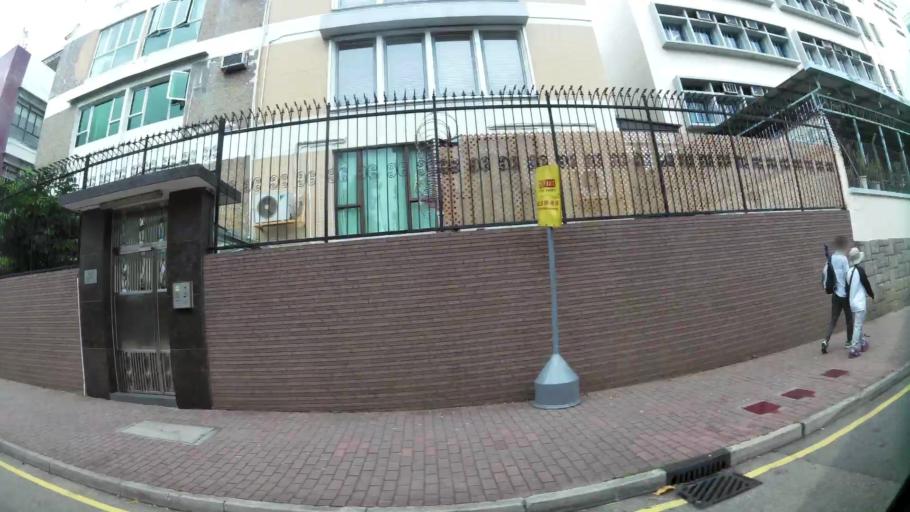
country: HK
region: Sham Shui Po
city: Sham Shui Po
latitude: 22.3308
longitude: 114.1752
